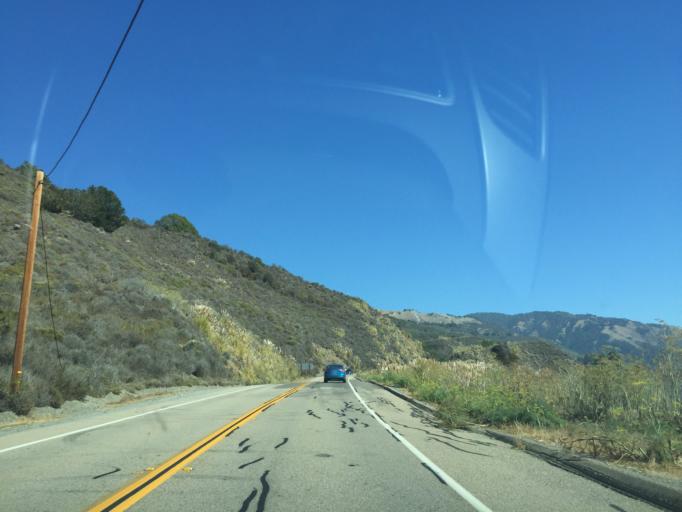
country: US
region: California
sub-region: Monterey County
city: Greenfield
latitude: 36.0215
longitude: -121.5629
